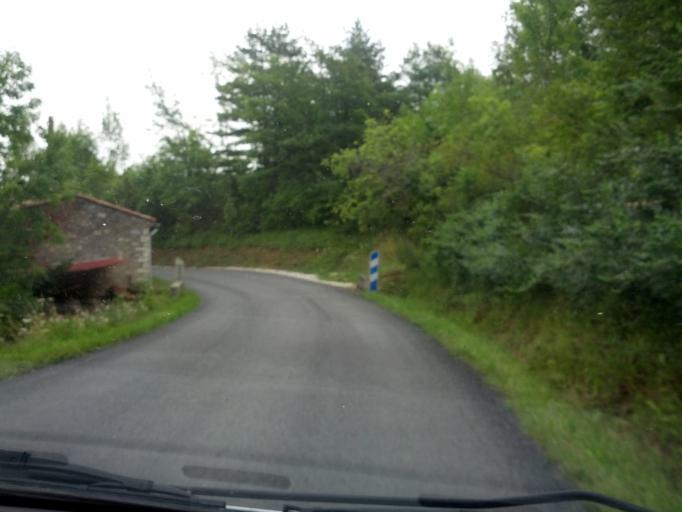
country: FR
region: Languedoc-Roussillon
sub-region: Departement de l'Aude
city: Quillan
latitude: 42.8861
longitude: 2.1512
